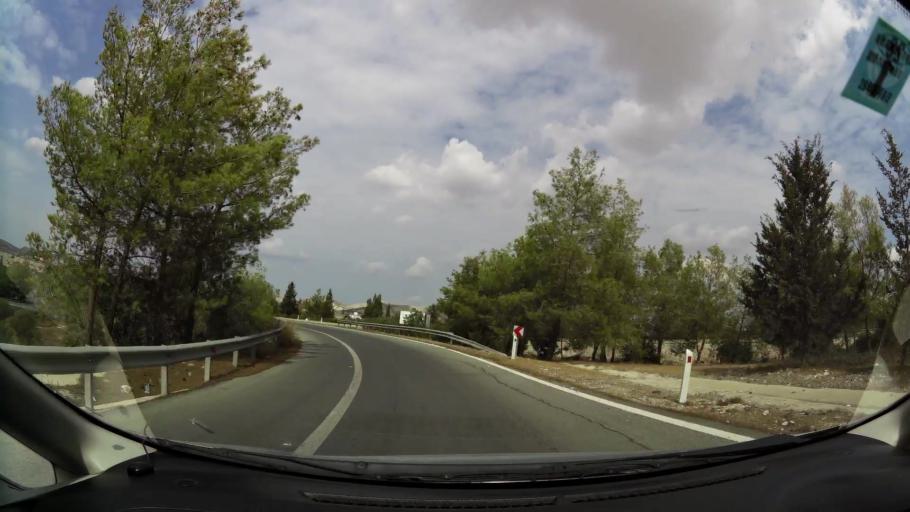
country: CY
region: Lefkosia
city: Lympia
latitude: 34.9905
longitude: 33.4599
